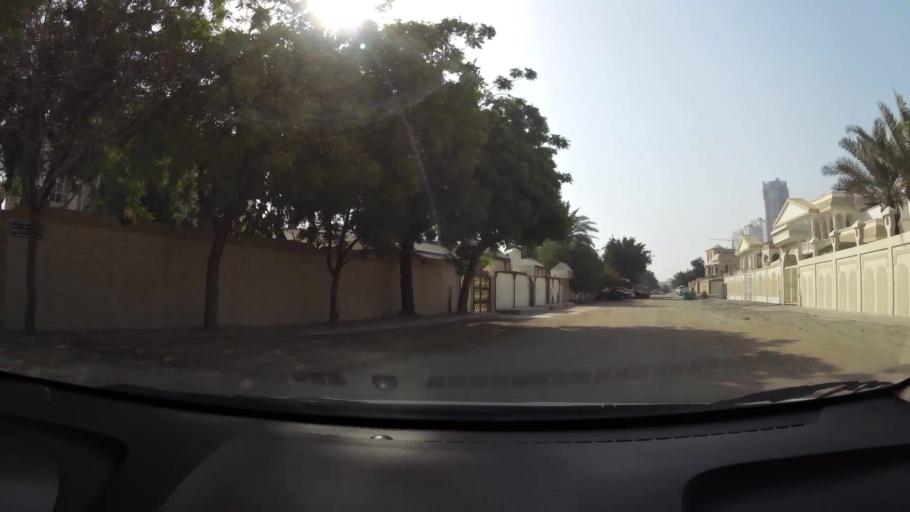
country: AE
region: Ajman
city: Ajman
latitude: 25.3873
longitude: 55.4337
